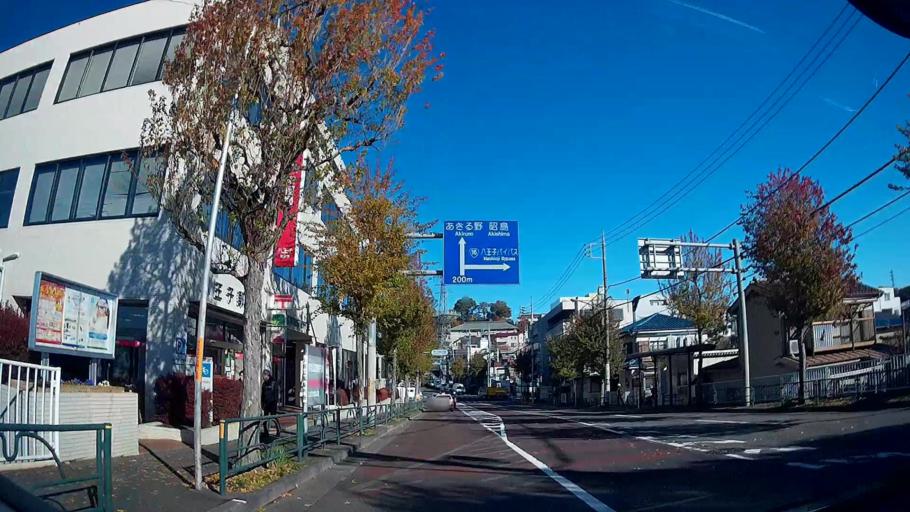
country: JP
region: Tokyo
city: Hachioji
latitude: 35.6665
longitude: 139.3410
